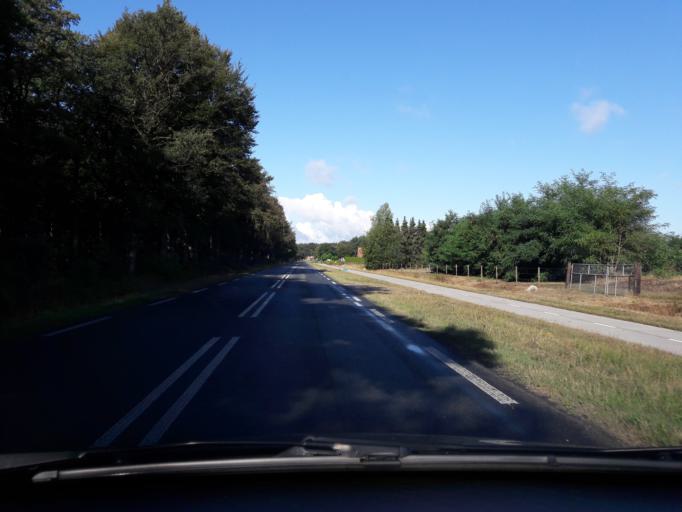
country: NL
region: Drenthe
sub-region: Gemeente Borger-Odoorn
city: Borger
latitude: 52.9091
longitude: 6.7170
